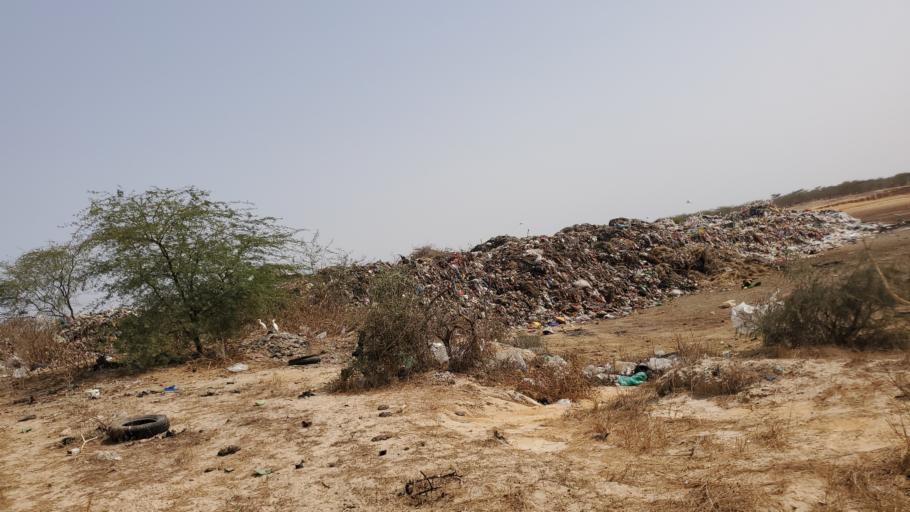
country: SN
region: Saint-Louis
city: Saint-Louis
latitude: 15.9479
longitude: -16.4306
